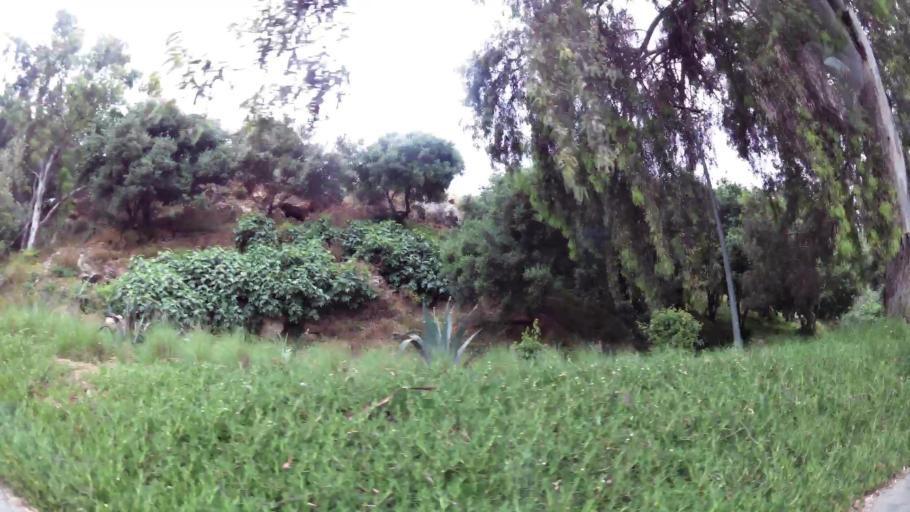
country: MA
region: Rabat-Sale-Zemmour-Zaer
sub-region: Rabat
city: Rabat
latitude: 34.0209
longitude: -6.8199
